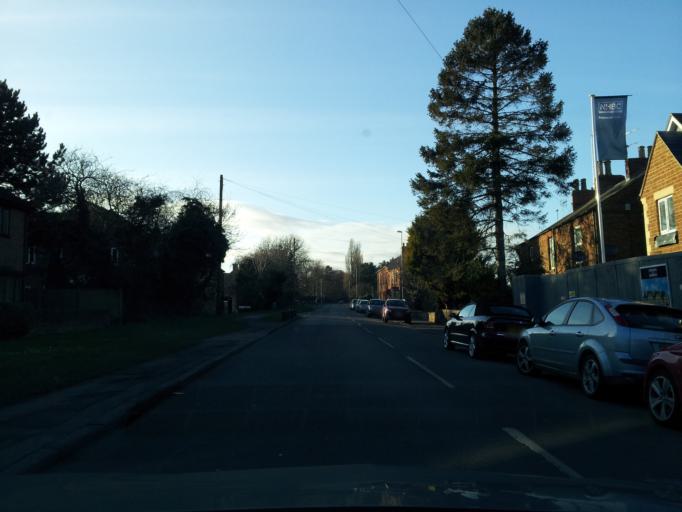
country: GB
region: England
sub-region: Northamptonshire
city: Northampton
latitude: 52.2592
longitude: -0.9535
